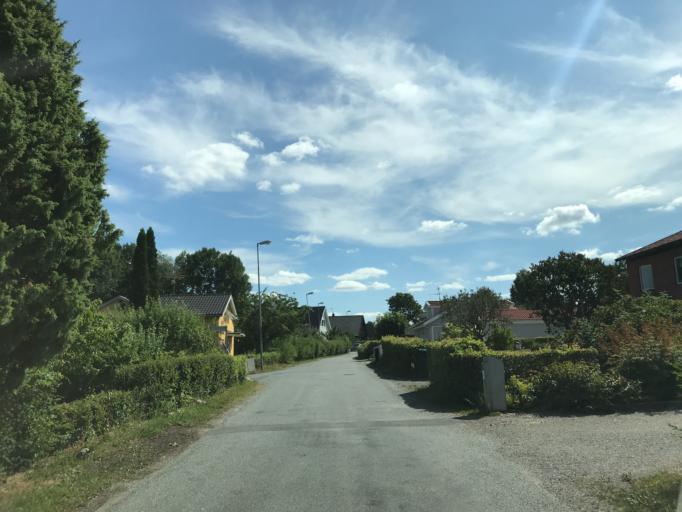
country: SE
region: Stockholm
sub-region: Upplands Vasby Kommun
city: Upplands Vaesby
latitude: 59.4830
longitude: 17.9031
